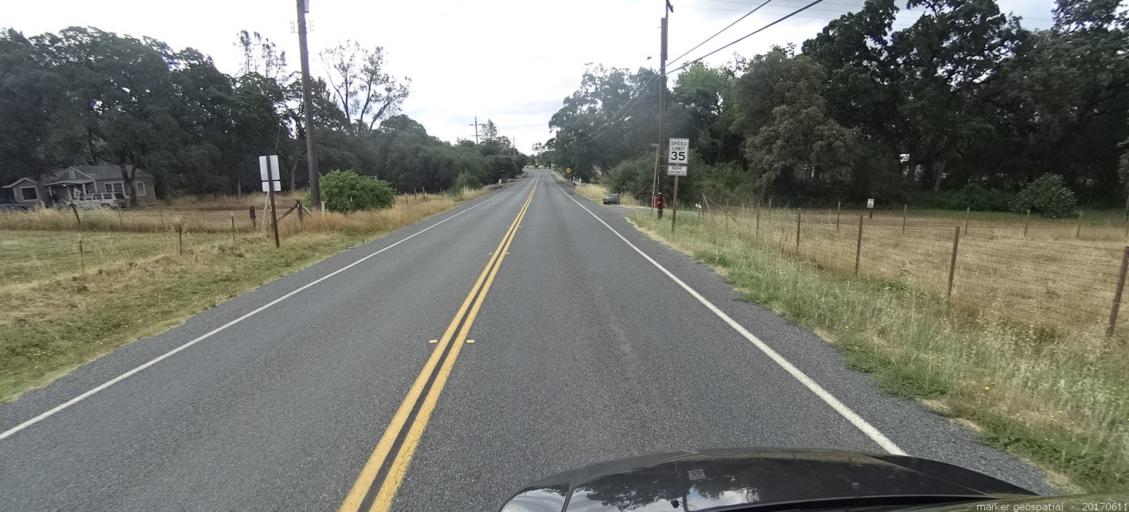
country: US
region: California
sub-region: Yuba County
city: Loma Rica
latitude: 39.3927
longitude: -121.4104
